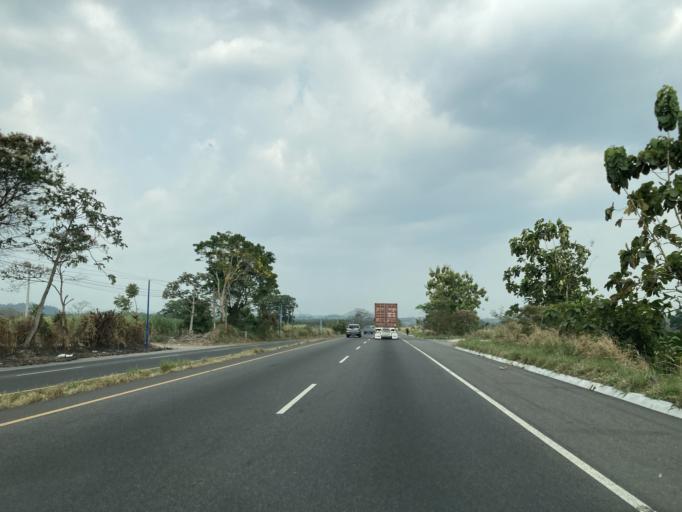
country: GT
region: Suchitepeque
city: Rio Bravo
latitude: 14.4098
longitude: -91.2819
